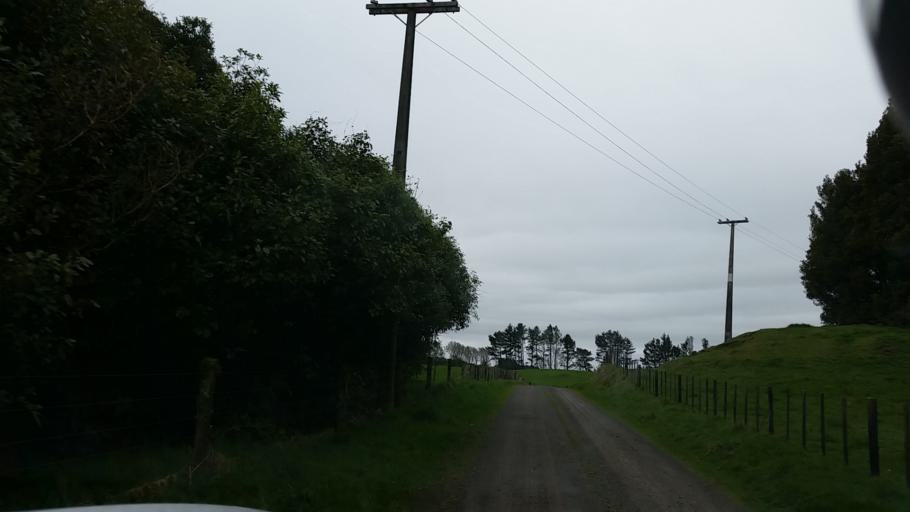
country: NZ
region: Bay of Plenty
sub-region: Rotorua District
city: Rotorua
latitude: -38.1024
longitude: 176.0684
